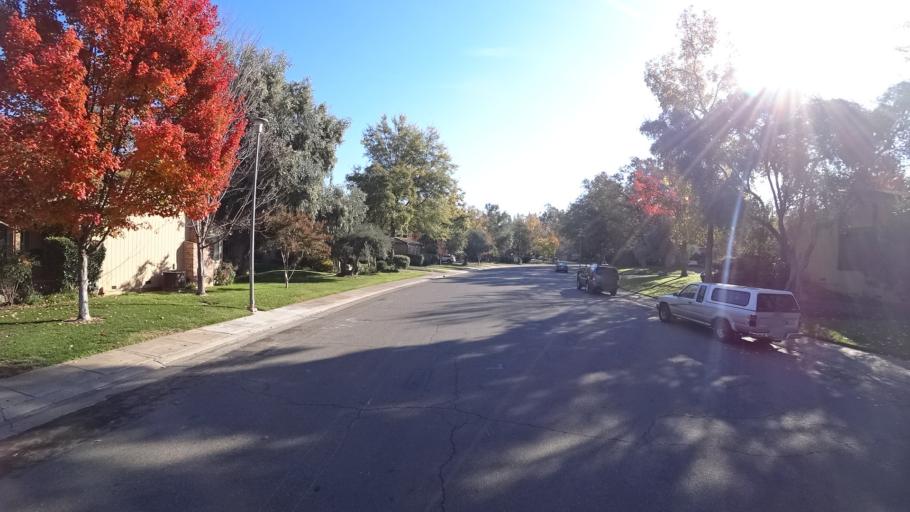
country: US
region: California
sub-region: Sacramento County
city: Citrus Heights
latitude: 38.6841
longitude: -121.3031
